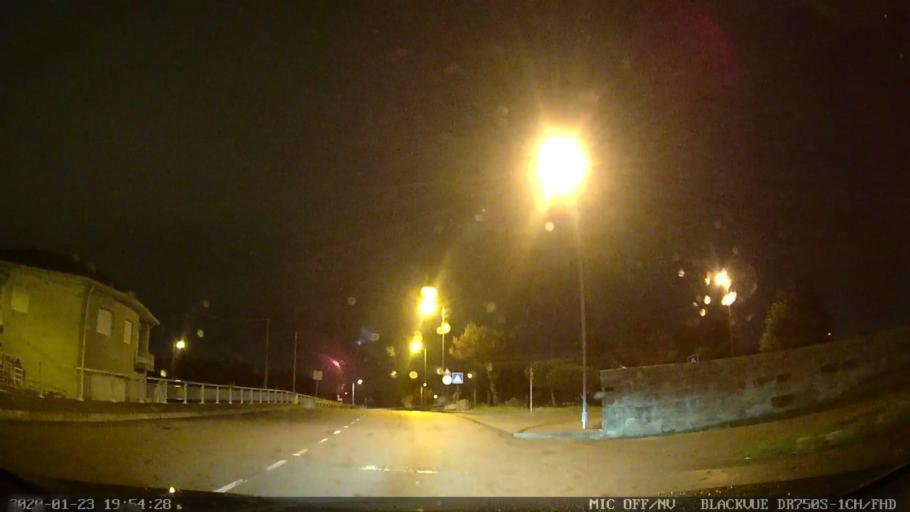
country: PT
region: Porto
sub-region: Matosinhos
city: Santa Cruz do Bispo
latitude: 41.2316
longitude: -8.6553
